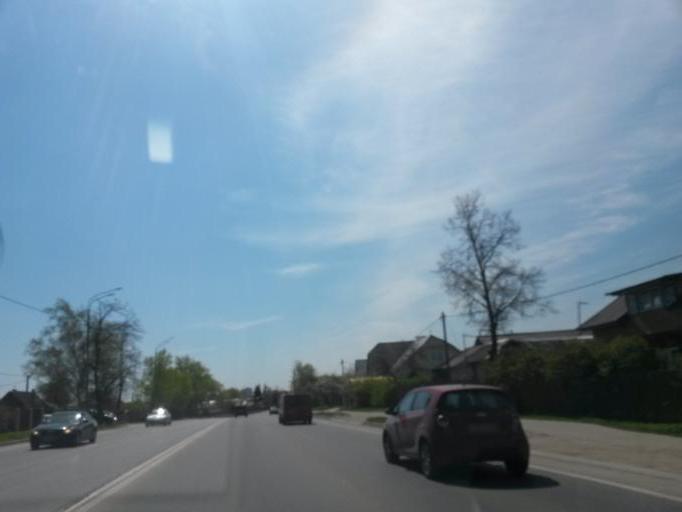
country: RU
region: Moskovskaya
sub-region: Podol'skiy Rayon
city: Podol'sk
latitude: 55.4012
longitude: 37.5515
